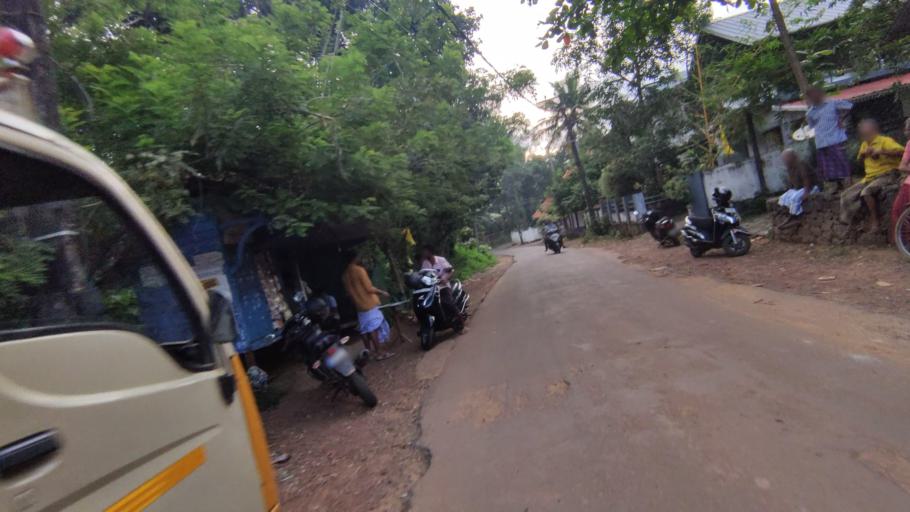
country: IN
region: Kerala
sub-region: Kottayam
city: Kottayam
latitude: 9.6344
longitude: 76.5044
